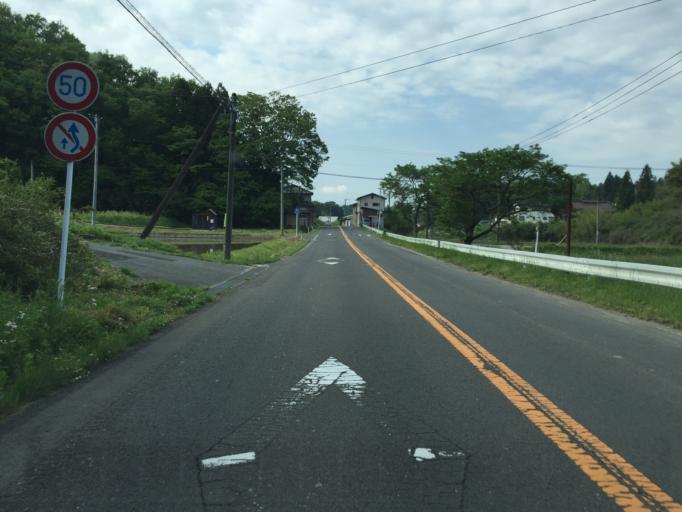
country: JP
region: Fukushima
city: Fukushima-shi
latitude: 37.6776
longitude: 140.5271
